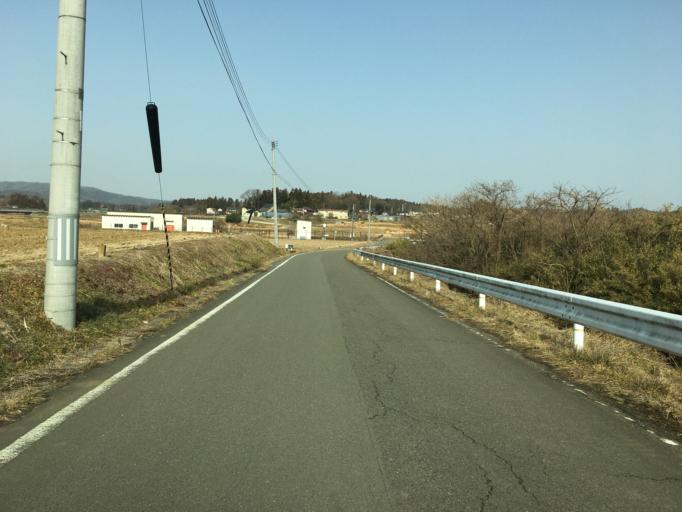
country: JP
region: Fukushima
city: Motomiya
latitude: 37.5570
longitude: 140.3973
